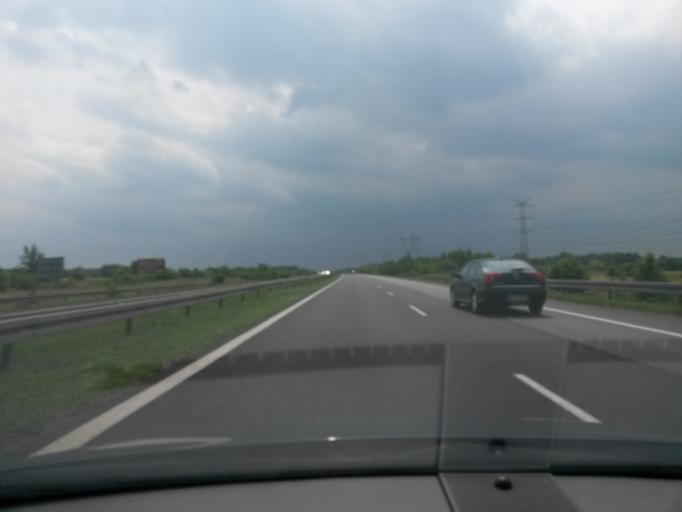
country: PL
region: Lodz Voivodeship
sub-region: Powiat radomszczanski
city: Radomsko
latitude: 51.0988
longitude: 19.3819
